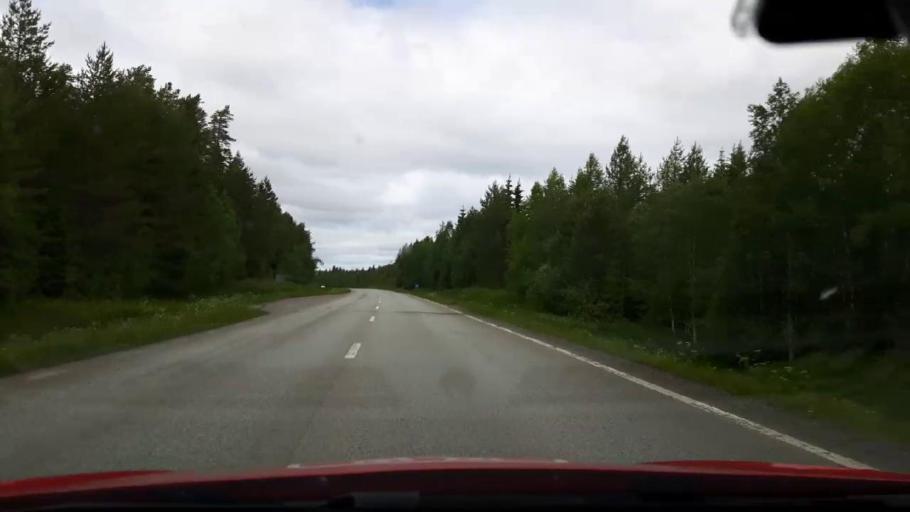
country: SE
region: Jaemtland
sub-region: Krokoms Kommun
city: Krokom
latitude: 63.3890
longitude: 14.5060
